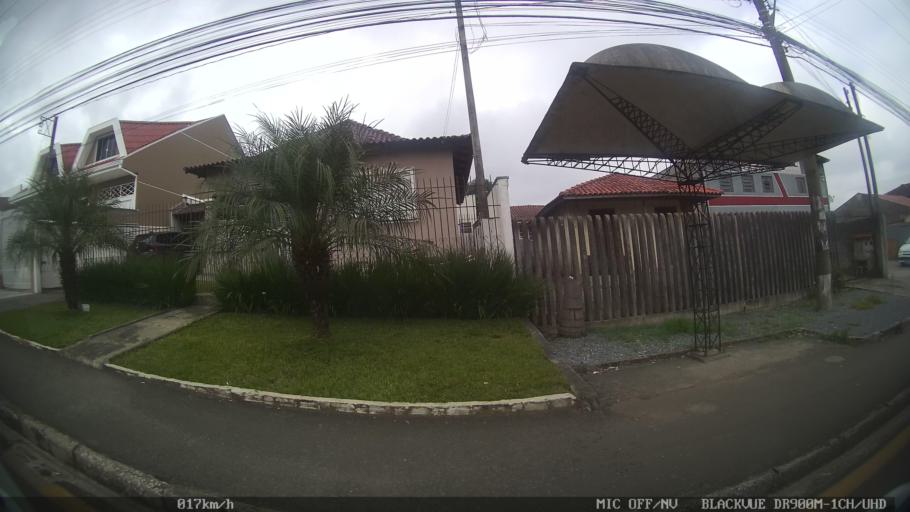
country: BR
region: Parana
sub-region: Curitiba
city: Curitiba
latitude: -25.3657
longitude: -49.2598
